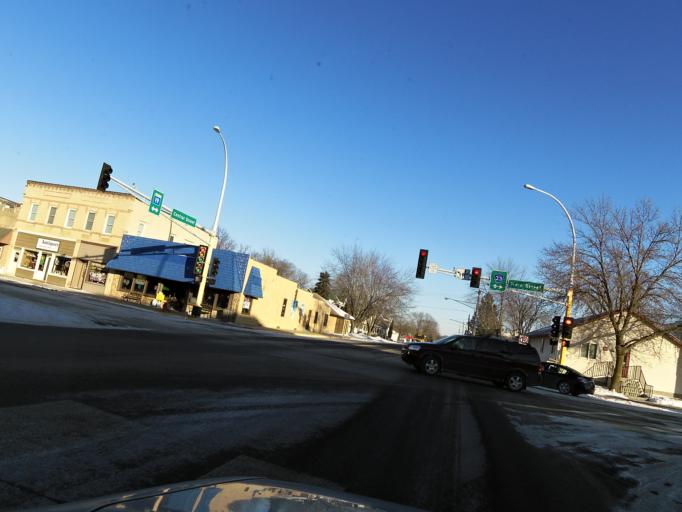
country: US
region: Minnesota
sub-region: Rice County
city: Lonsdale
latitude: 44.4806
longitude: -93.4288
